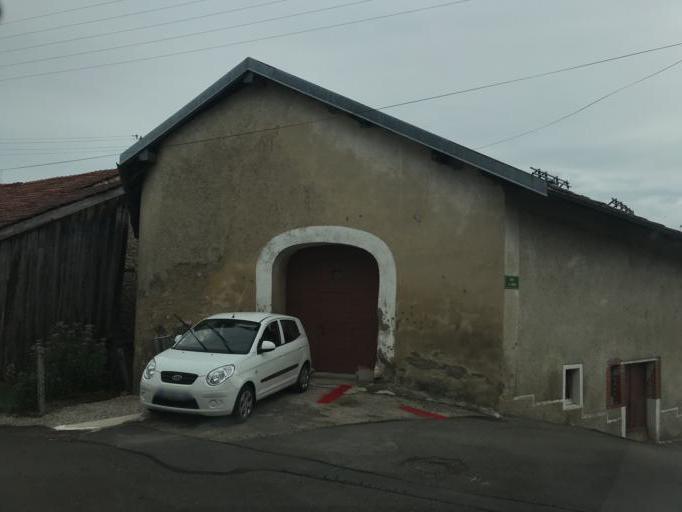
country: FR
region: Franche-Comte
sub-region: Departement du Jura
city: Lavans-les-Saint-Claude
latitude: 46.3268
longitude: 5.7487
